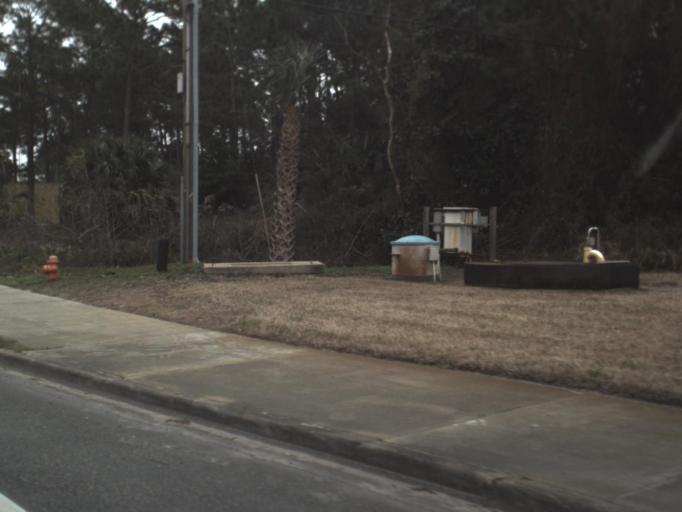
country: US
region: Florida
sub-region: Bay County
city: Panama City Beach
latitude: 30.1842
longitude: -85.7785
